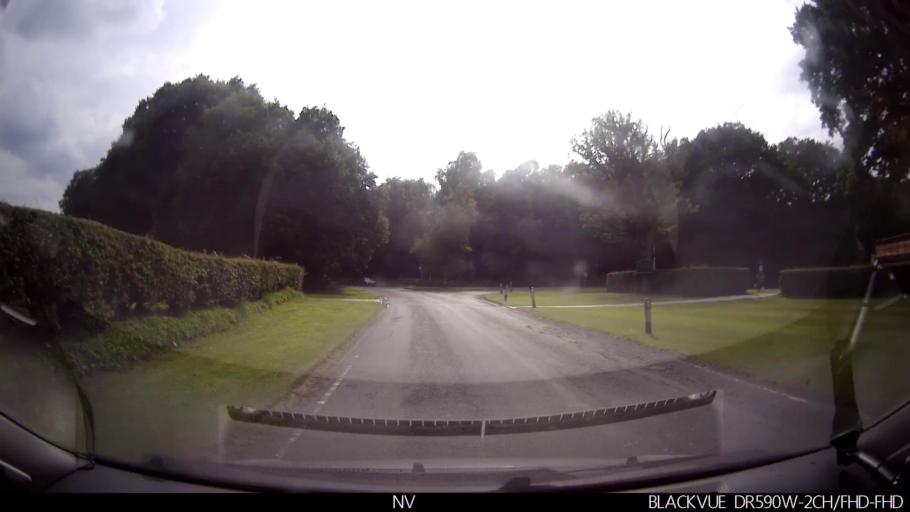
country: GB
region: England
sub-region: North Yorkshire
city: Strensall
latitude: 54.0370
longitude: -1.0226
